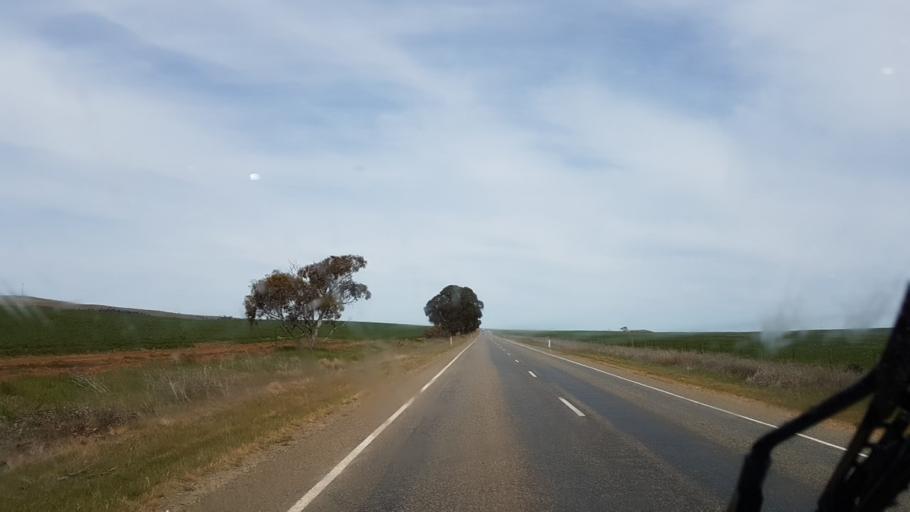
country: AU
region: South Australia
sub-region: Northern Areas
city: Jamestown
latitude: -33.0947
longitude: 138.6198
